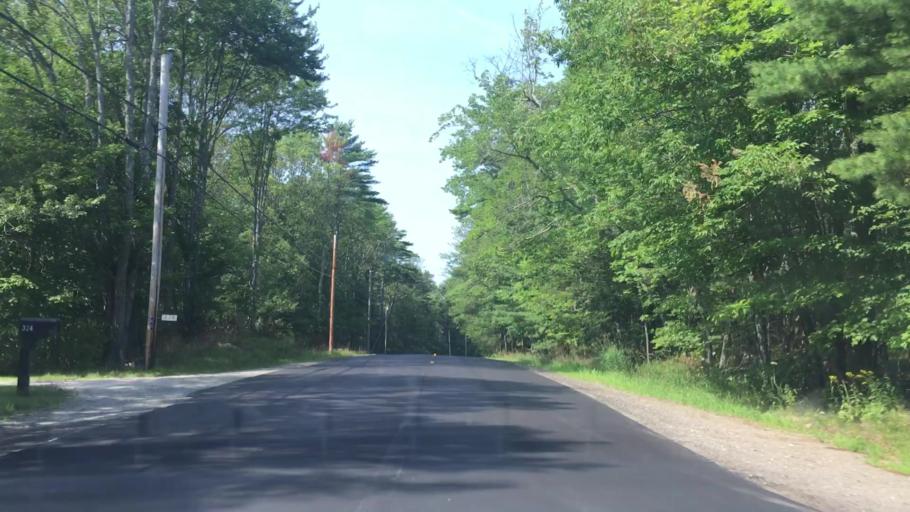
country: US
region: Maine
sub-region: Sagadahoc County
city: North Bath
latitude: 43.9386
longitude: -69.8000
